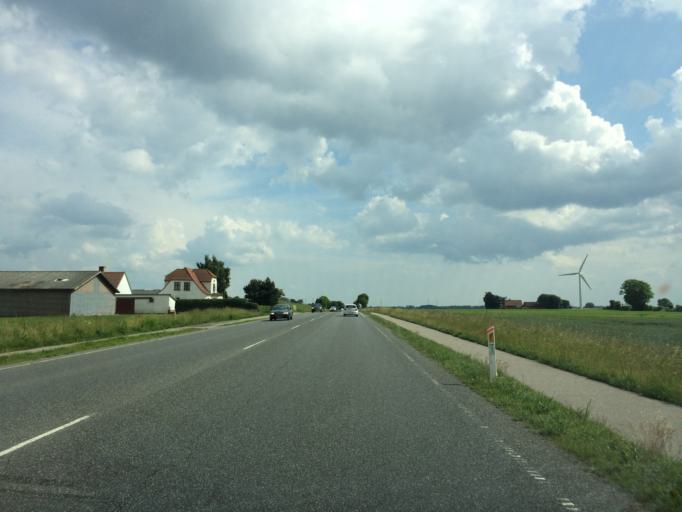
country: DK
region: South Denmark
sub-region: Fredericia Kommune
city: Taulov
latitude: 55.5792
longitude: 9.6607
